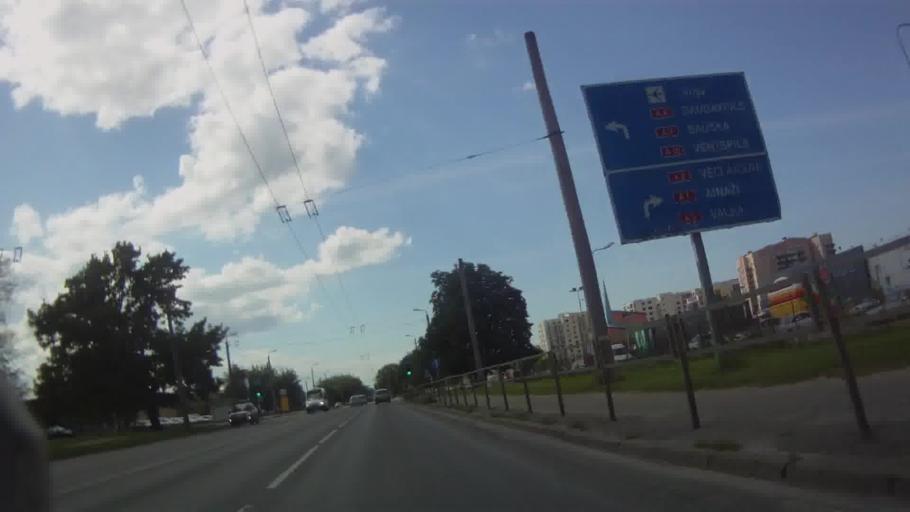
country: LV
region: Riga
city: Riga
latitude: 56.9488
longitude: 24.1890
